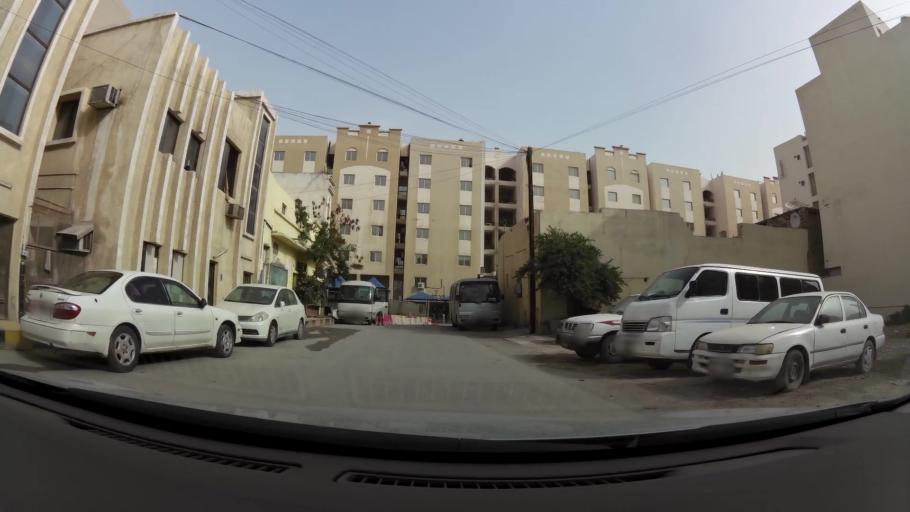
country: QA
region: Baladiyat ad Dawhah
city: Doha
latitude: 25.2822
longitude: 51.5470
